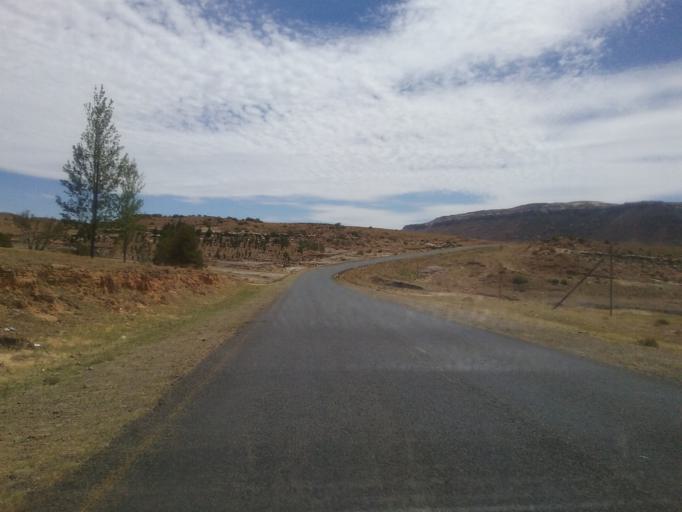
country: LS
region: Mafeteng
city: Mafeteng
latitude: -29.9030
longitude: 27.2515
